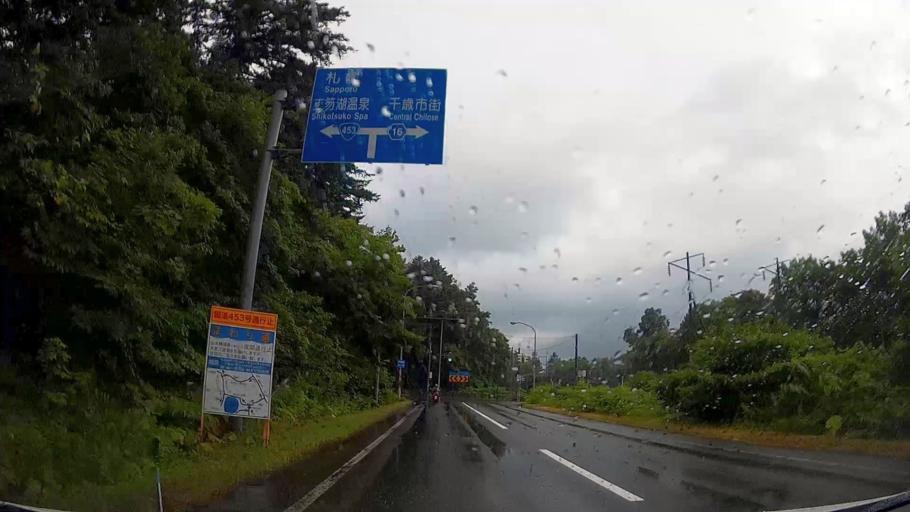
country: JP
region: Hokkaido
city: Tomakomai
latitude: 42.7635
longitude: 141.4354
